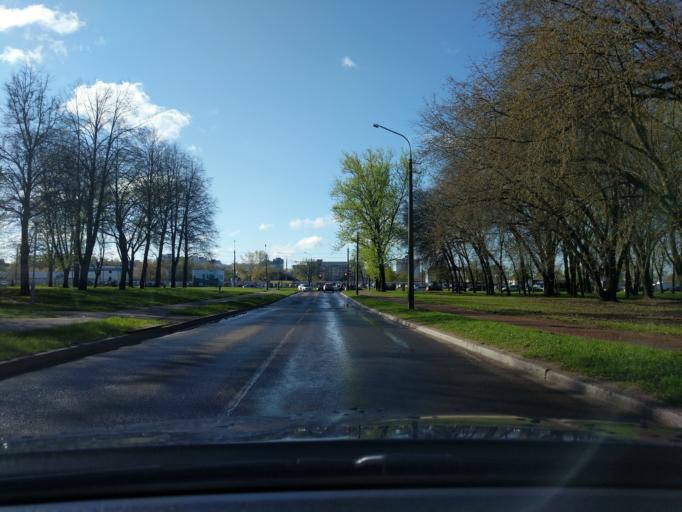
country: BY
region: Minsk
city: Novoye Medvezhino
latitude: 53.8993
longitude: 27.5068
